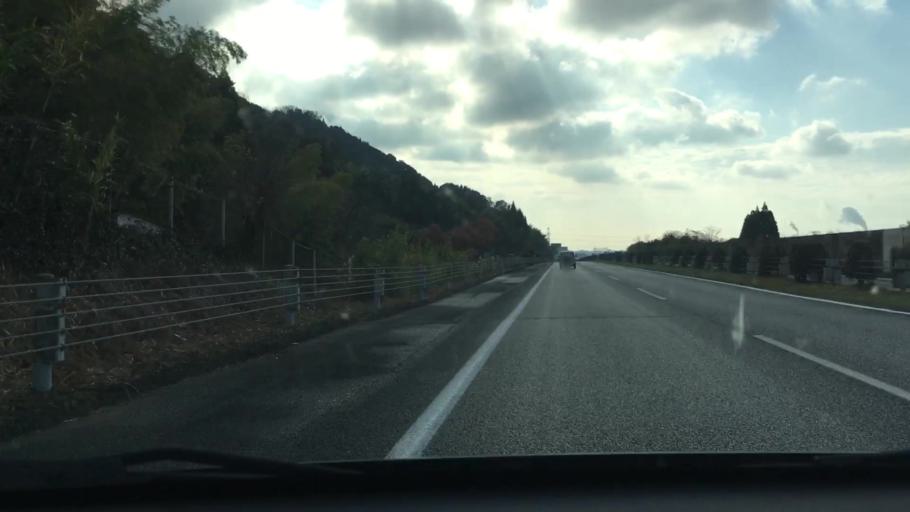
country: JP
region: Kumamoto
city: Yatsushiro
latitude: 32.5292
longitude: 130.6669
